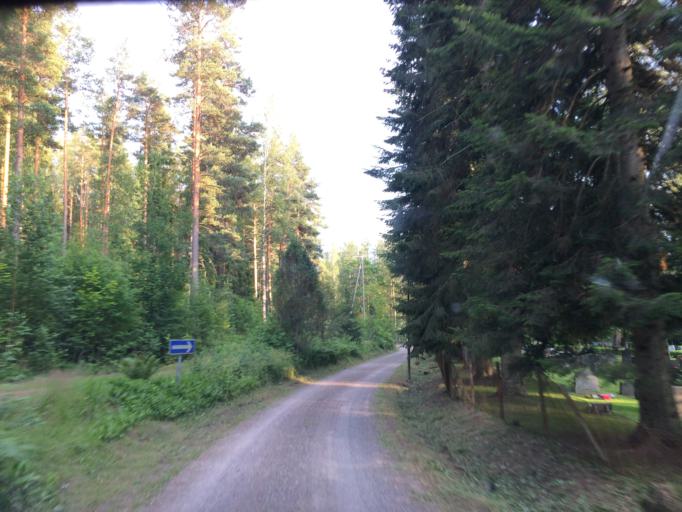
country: FI
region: Haeme
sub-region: Haemeenlinna
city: Janakkala
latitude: 60.8936
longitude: 24.5997
